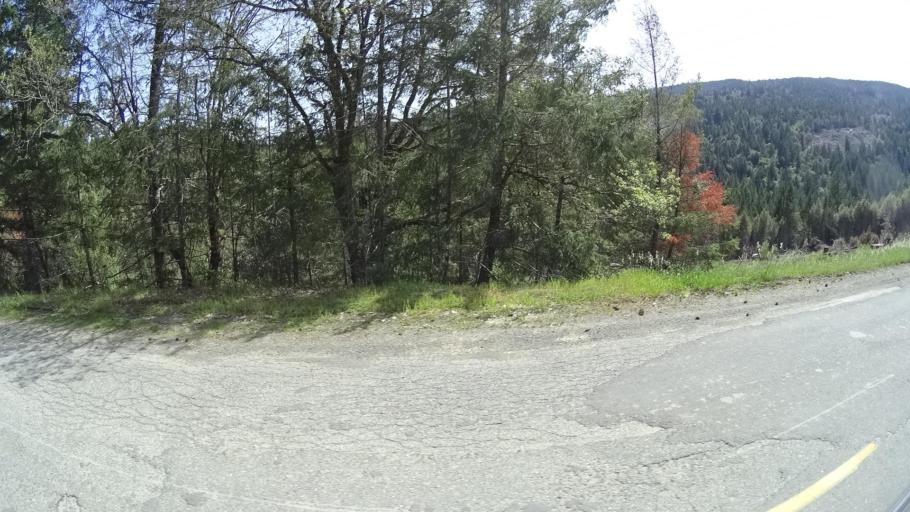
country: US
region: California
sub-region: Humboldt County
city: Redway
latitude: 40.3685
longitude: -123.7324
